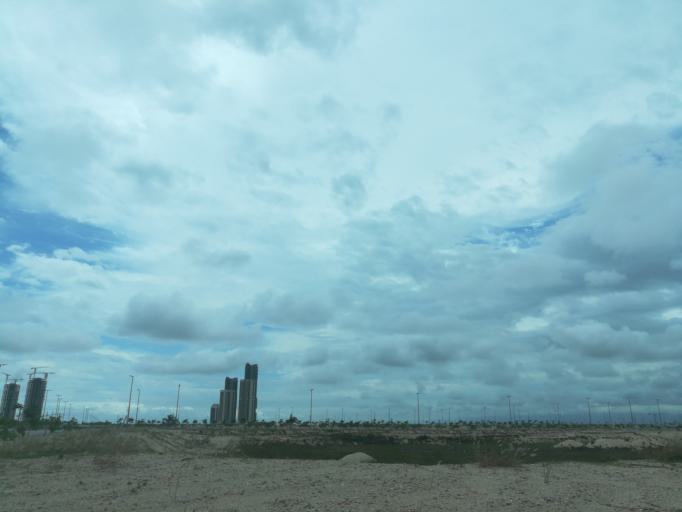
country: NG
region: Lagos
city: Ikoyi
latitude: 6.4108
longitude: 3.4213
